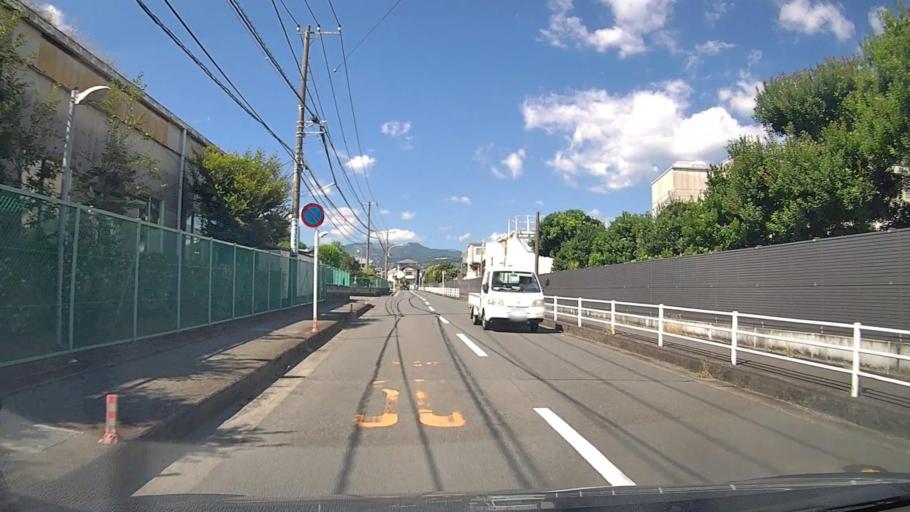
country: JP
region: Kanagawa
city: Odawara
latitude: 35.3319
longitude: 139.1283
